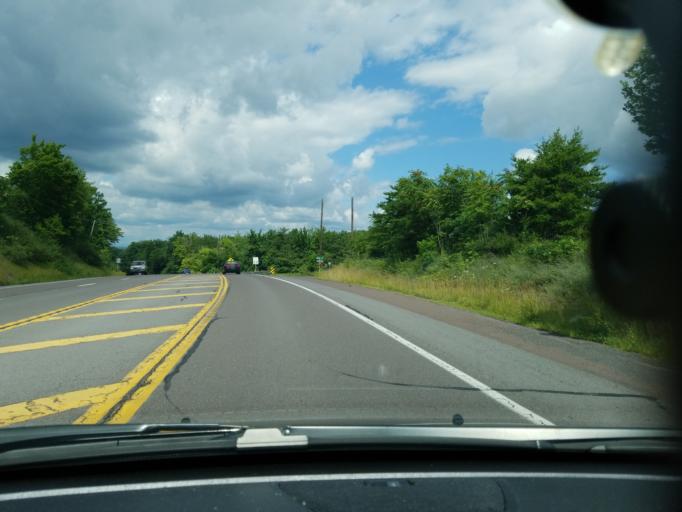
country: US
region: Pennsylvania
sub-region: Northumberland County
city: Elysburg
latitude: 40.8484
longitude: -76.5258
